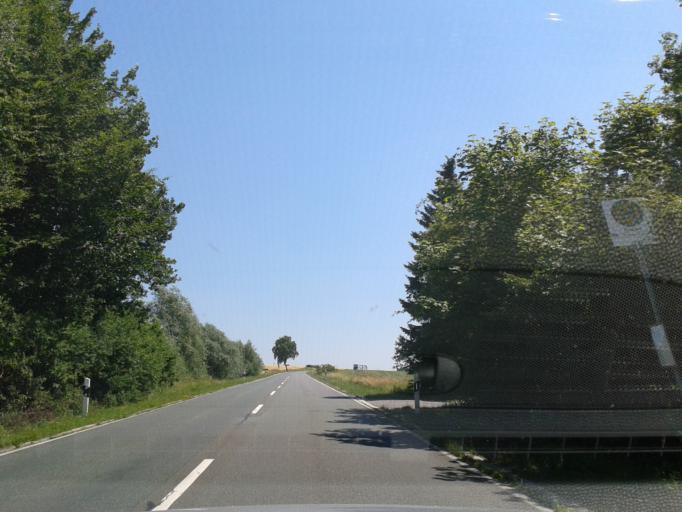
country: DE
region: North Rhine-Westphalia
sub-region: Regierungsbezirk Detmold
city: Barntrup
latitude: 51.9750
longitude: 9.1751
